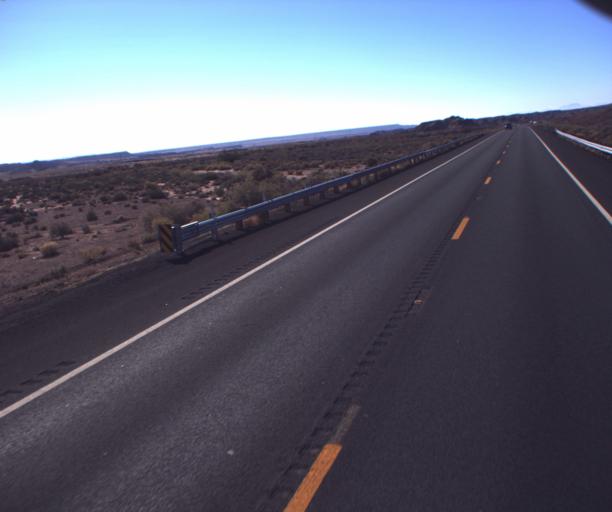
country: US
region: Arizona
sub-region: Coconino County
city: Tuba City
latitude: 36.1153
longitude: -111.3952
